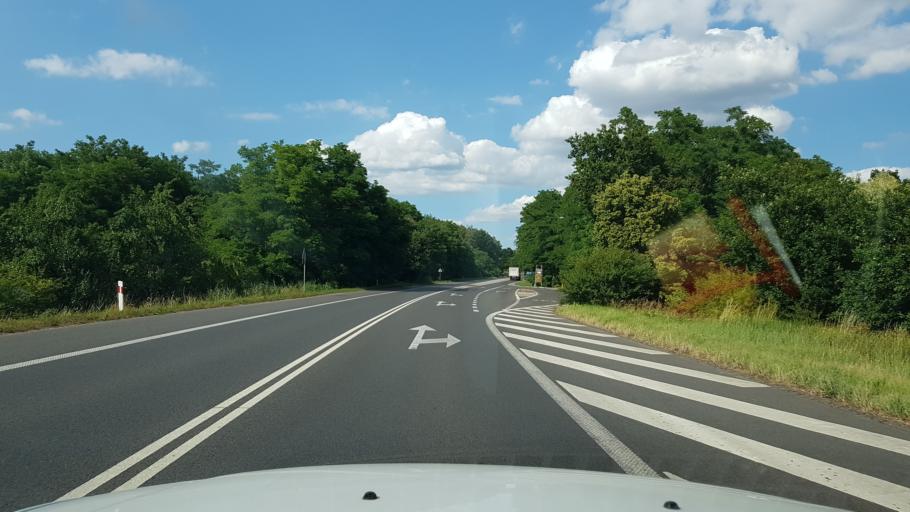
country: PL
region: West Pomeranian Voivodeship
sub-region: Powiat gryfinski
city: Stare Czarnowo
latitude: 53.2498
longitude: 14.7810
